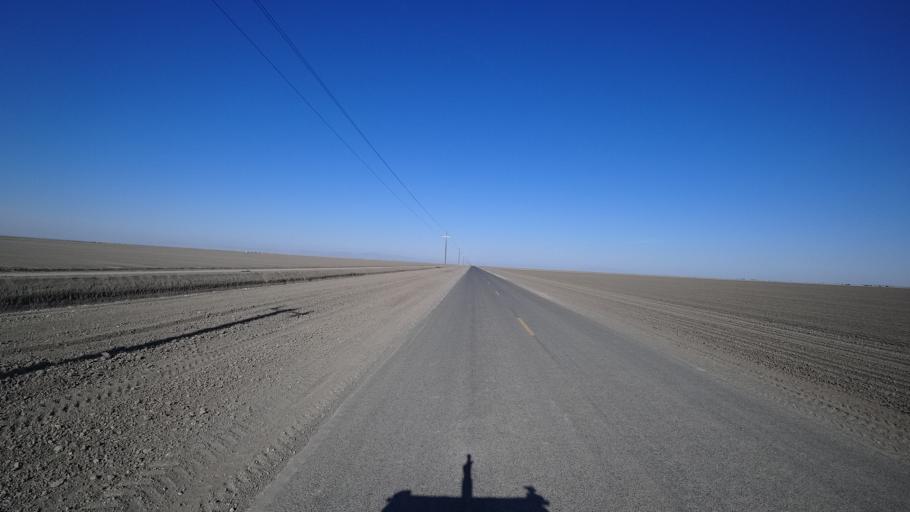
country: US
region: California
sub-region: Kings County
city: Corcoran
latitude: 36.0797
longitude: -119.7016
